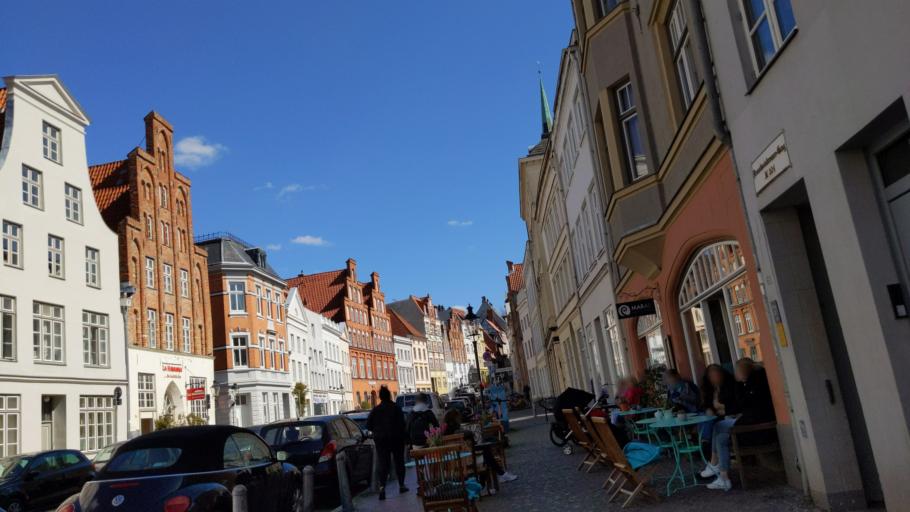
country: DE
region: Schleswig-Holstein
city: Luebeck
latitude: 53.8719
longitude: 10.6851
